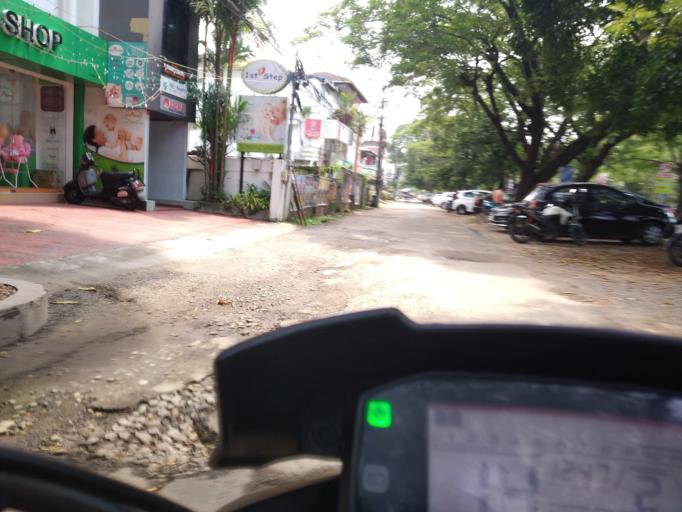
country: IN
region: Kerala
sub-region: Ernakulam
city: Cochin
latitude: 9.9587
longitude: 76.2961
